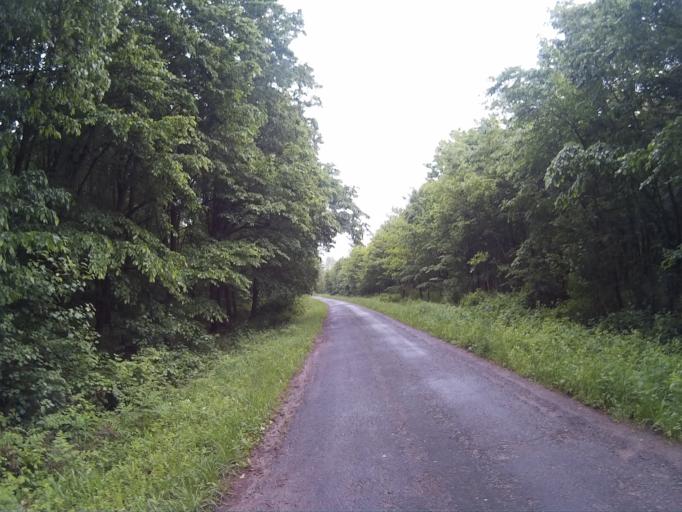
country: HU
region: Veszprem
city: Sumeg
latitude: 46.9158
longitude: 17.2815
